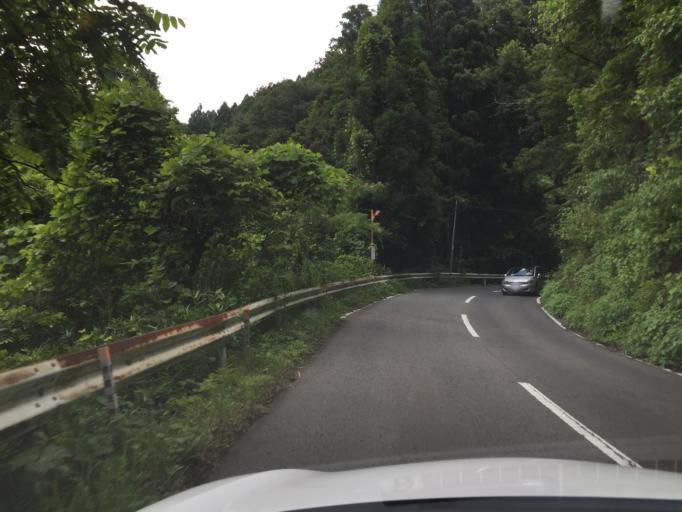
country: JP
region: Fukushima
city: Iwaki
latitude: 37.0298
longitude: 140.7080
